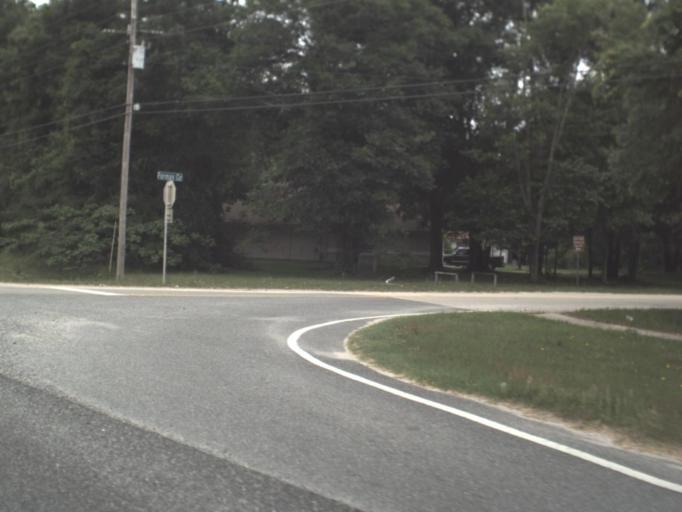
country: US
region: Florida
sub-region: Clay County
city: Middleburg
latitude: 30.0497
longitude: -81.8890
